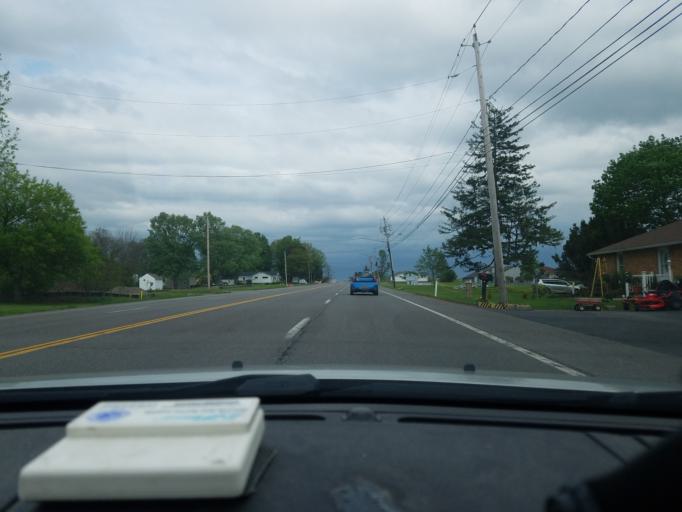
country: US
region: New York
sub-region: Onondaga County
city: Galeville
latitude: 43.1212
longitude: -76.1768
